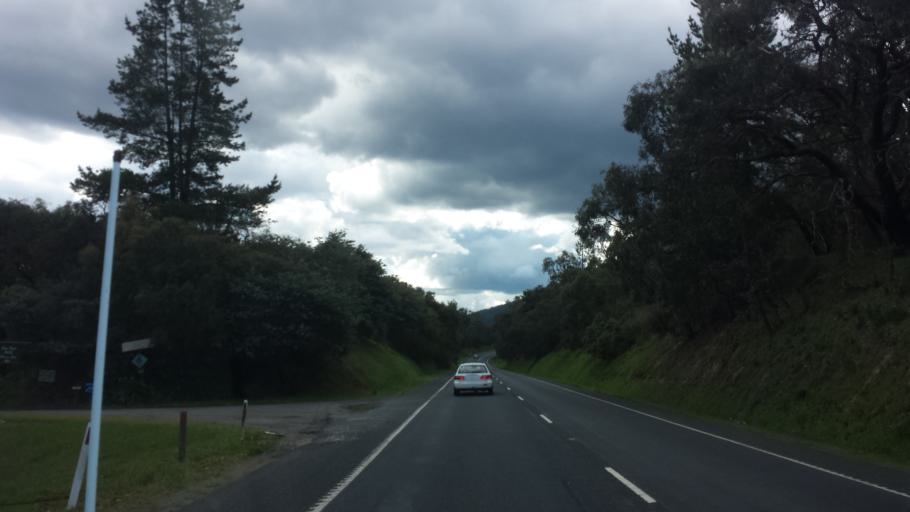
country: AU
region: Victoria
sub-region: Yarra Ranges
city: Selby
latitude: -37.9447
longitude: 145.3832
